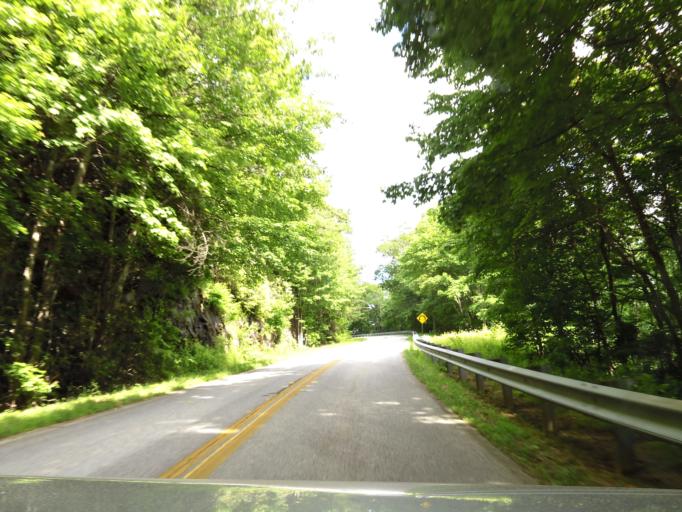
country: US
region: Georgia
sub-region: Towns County
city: Hiawassee
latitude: 34.8605
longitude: -83.8007
